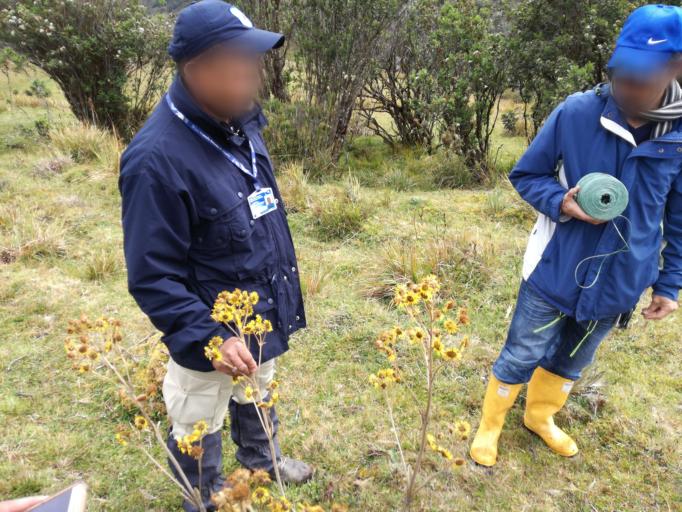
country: CO
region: Boyaca
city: Socha Viejo
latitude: 5.8959
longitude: -72.6778
